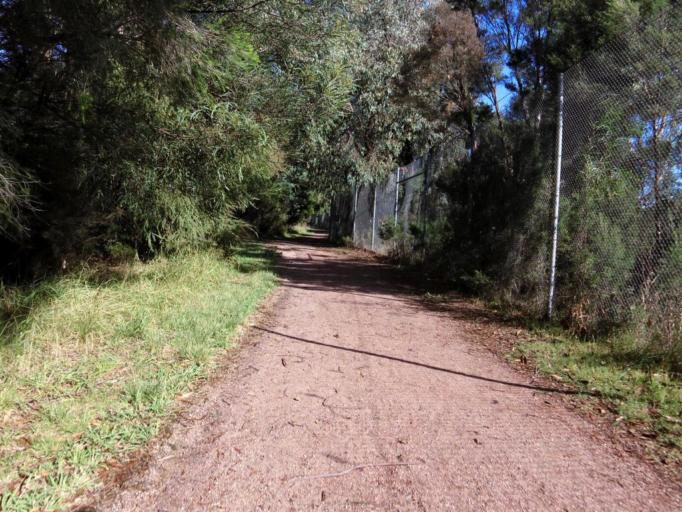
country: AU
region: Victoria
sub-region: Maroondah
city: Bayswater North
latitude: -37.8108
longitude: 145.3014
